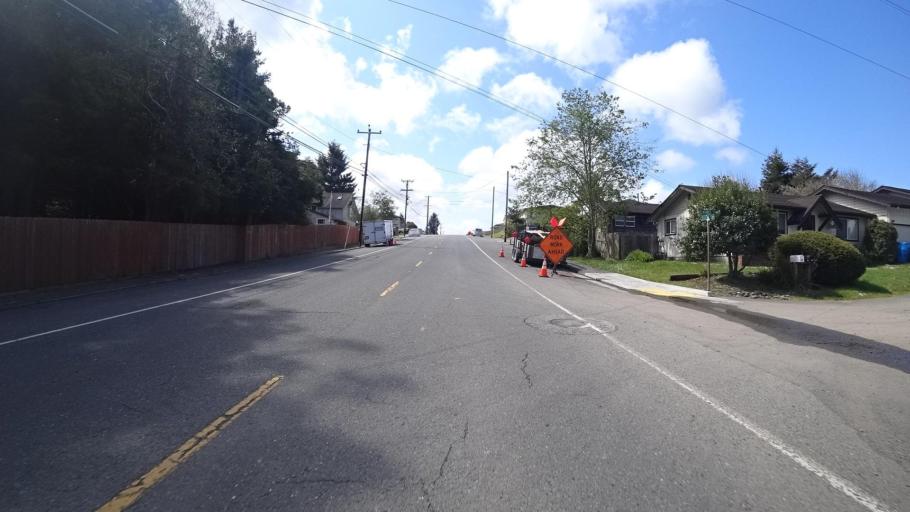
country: US
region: California
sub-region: Humboldt County
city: Bayview
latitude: 40.7680
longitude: -124.1637
